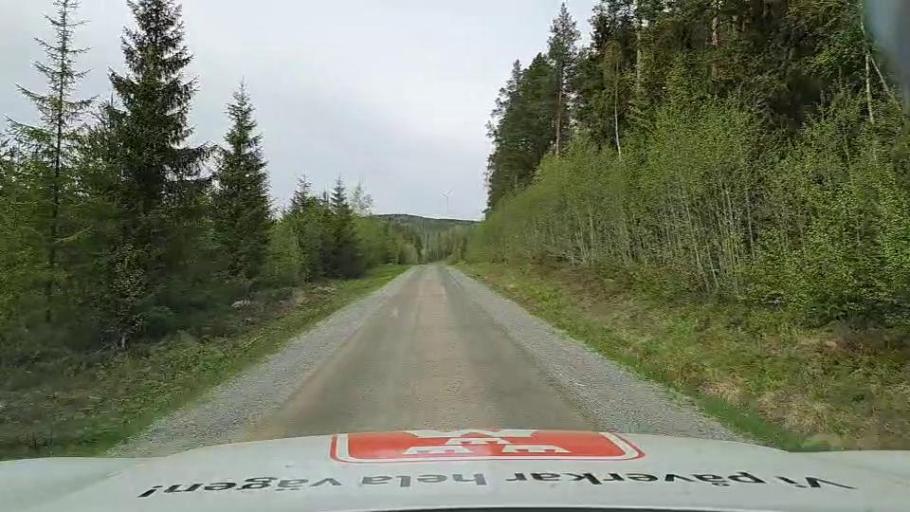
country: SE
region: Jaemtland
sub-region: Bergs Kommun
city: Hoverberg
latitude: 62.5234
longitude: 14.9136
